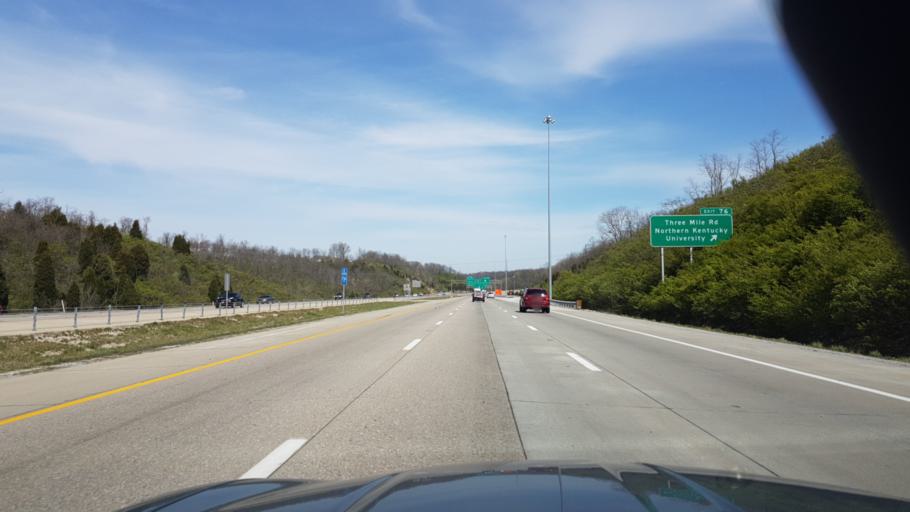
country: US
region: Kentucky
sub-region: Campbell County
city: Highland Heights
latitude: 39.0340
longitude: -84.4704
